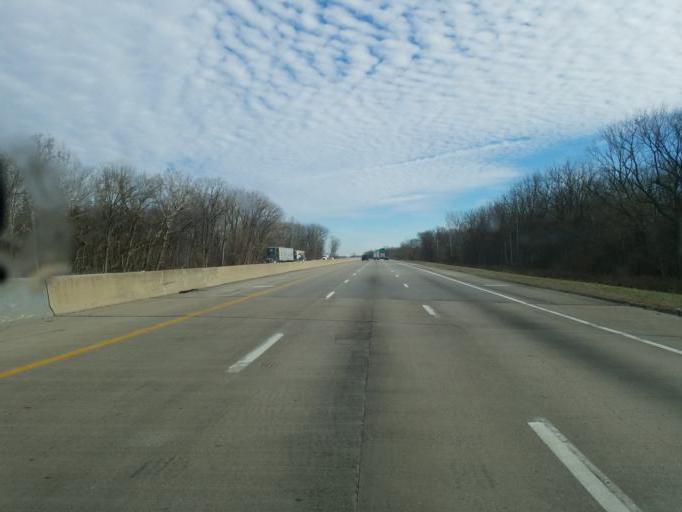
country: US
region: Ohio
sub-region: Clark County
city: Crystal Lakes
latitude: 39.8645
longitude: -84.0228
